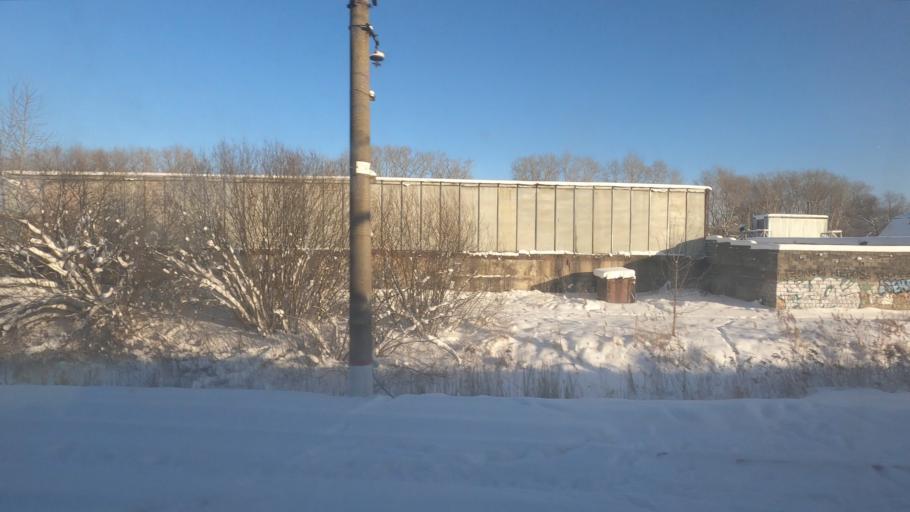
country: RU
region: Moskovskaya
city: Dmitrov
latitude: 56.3816
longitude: 37.5175
